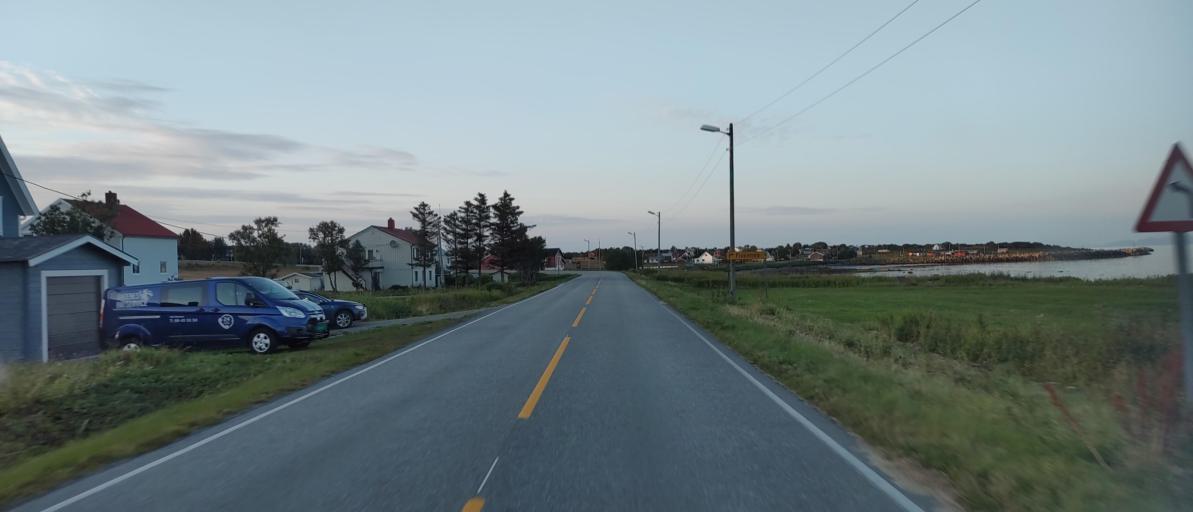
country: NO
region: Nordland
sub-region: Andoy
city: Andenes
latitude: 69.2427
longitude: 16.1168
